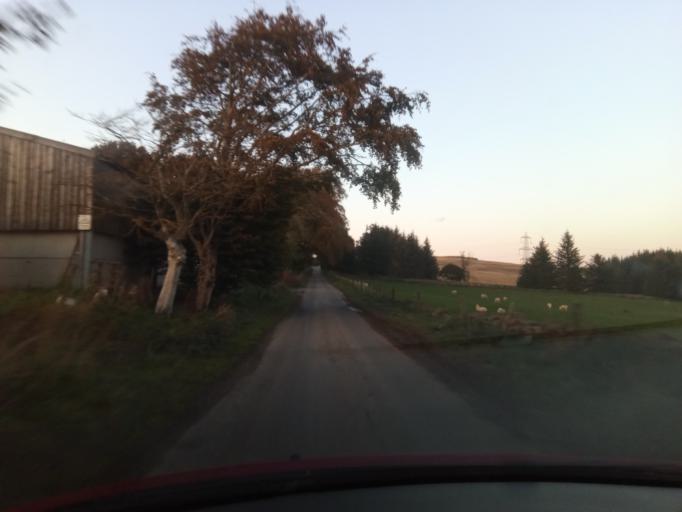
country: GB
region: Scotland
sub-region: East Lothian
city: Pencaitland
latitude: 55.7983
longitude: -2.8885
